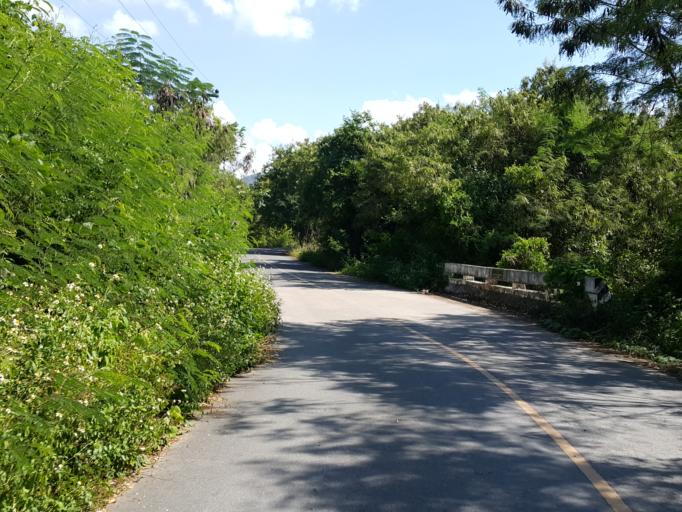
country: TH
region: Chiang Mai
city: San Sai
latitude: 18.8656
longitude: 99.1585
